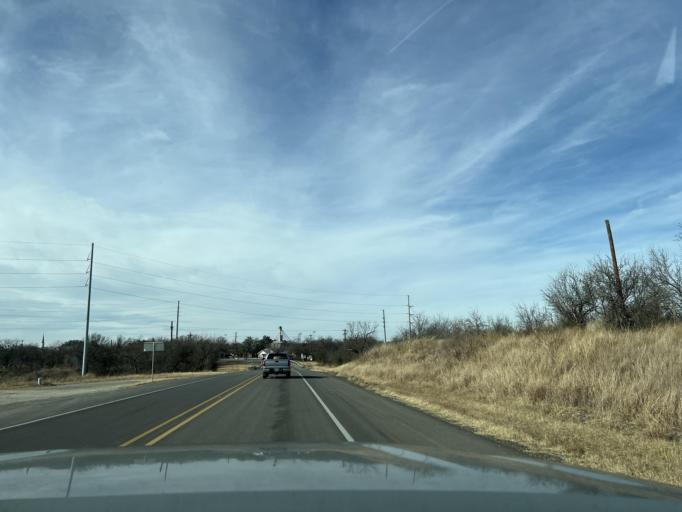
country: US
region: Texas
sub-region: Shackelford County
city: Albany
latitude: 32.7218
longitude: -99.2916
